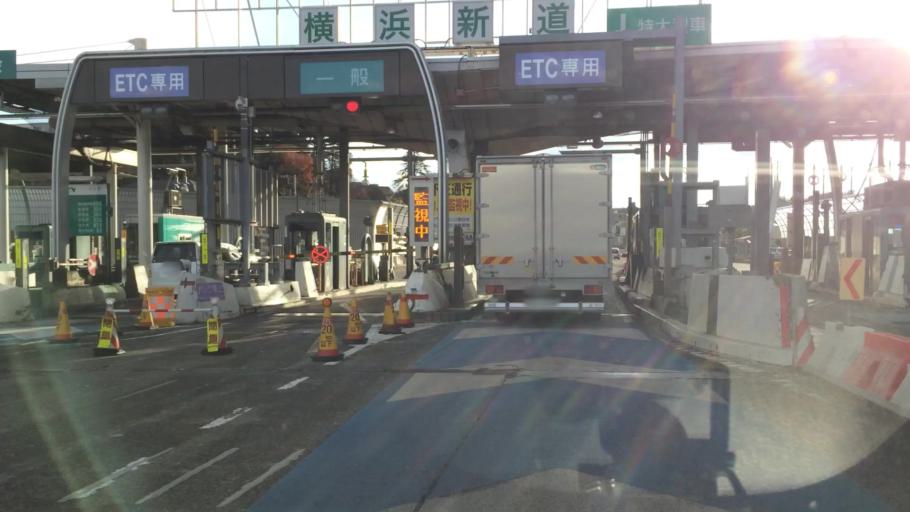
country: JP
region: Kanagawa
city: Yokohama
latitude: 35.4231
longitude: 139.5396
